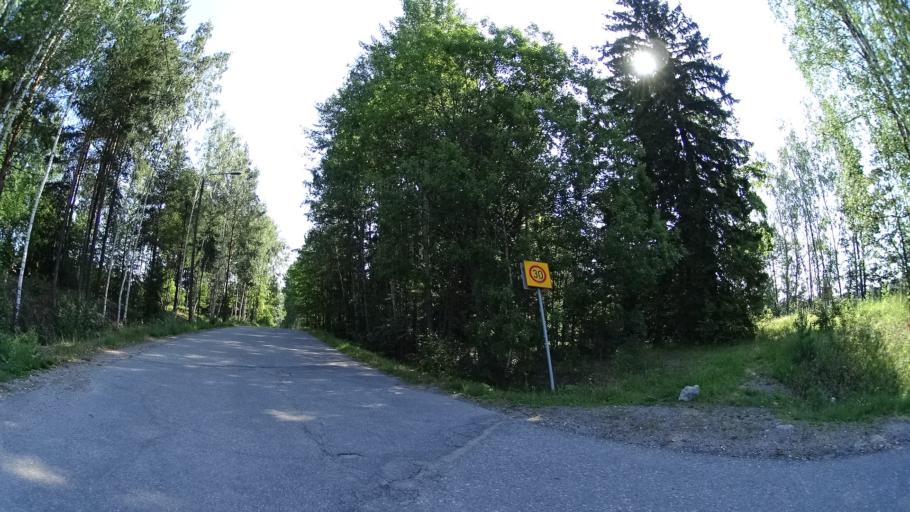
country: FI
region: Uusimaa
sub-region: Helsinki
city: Vantaa
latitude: 60.3147
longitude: 25.0787
